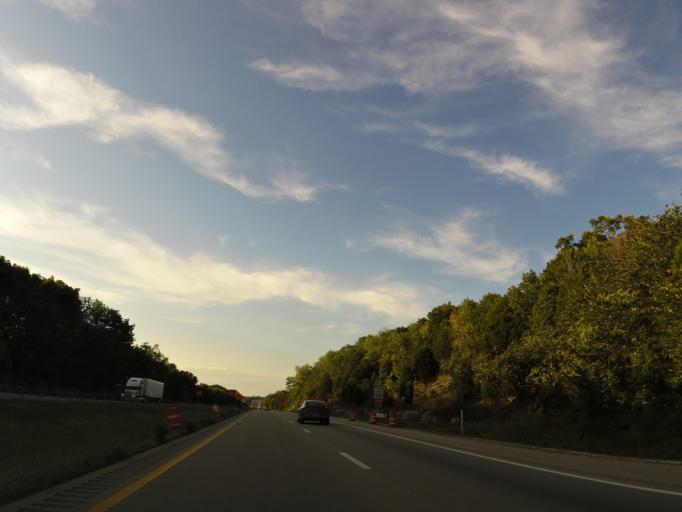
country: US
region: Kentucky
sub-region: Rockcastle County
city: Mount Vernon
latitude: 37.4031
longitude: -84.3388
